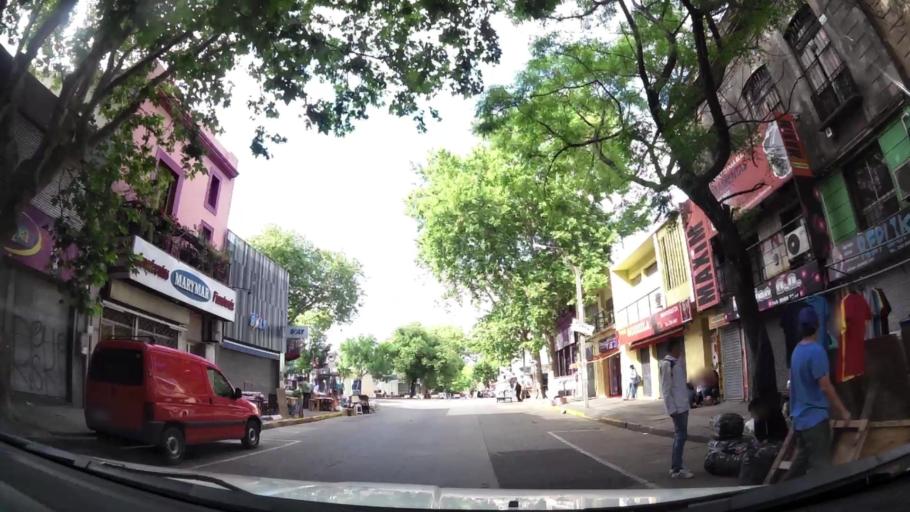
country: UY
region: Montevideo
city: Montevideo
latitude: -34.8854
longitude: -56.1795
